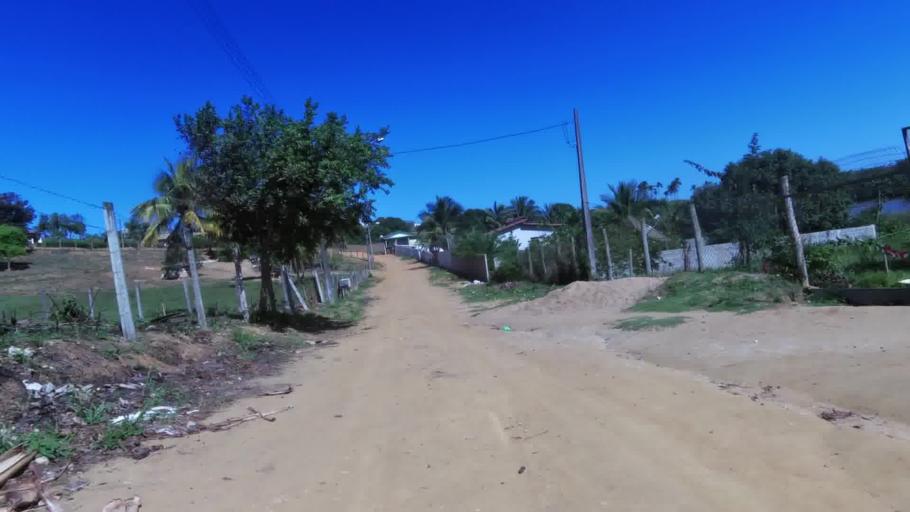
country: BR
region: Espirito Santo
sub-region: Guarapari
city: Guarapari
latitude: -20.7361
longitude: -40.5577
